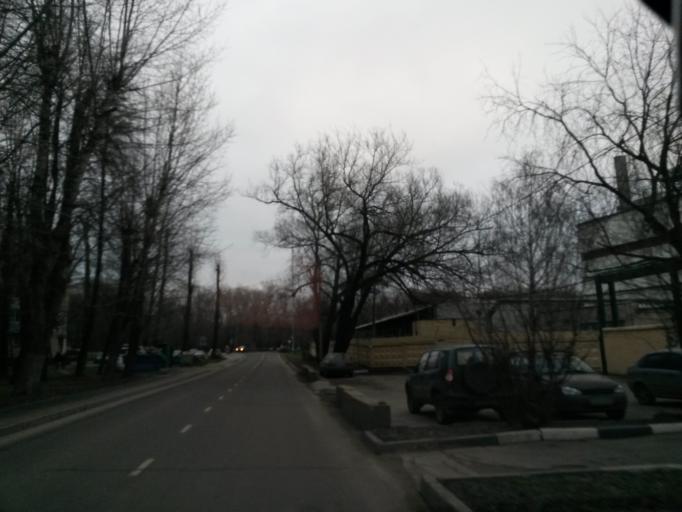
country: RU
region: Moskovskaya
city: Bol'shaya Setun'
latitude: 55.7149
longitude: 37.4356
